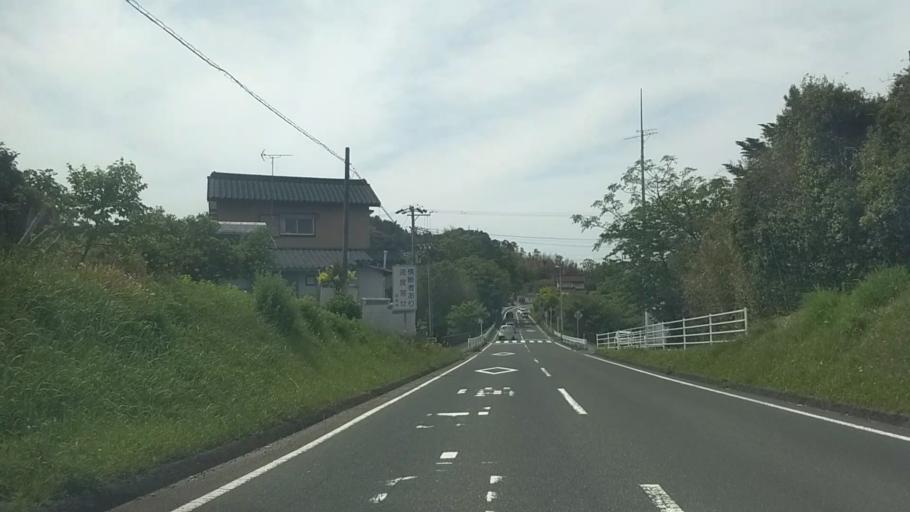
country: JP
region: Shizuoka
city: Kosai-shi
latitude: 34.7904
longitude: 137.5831
